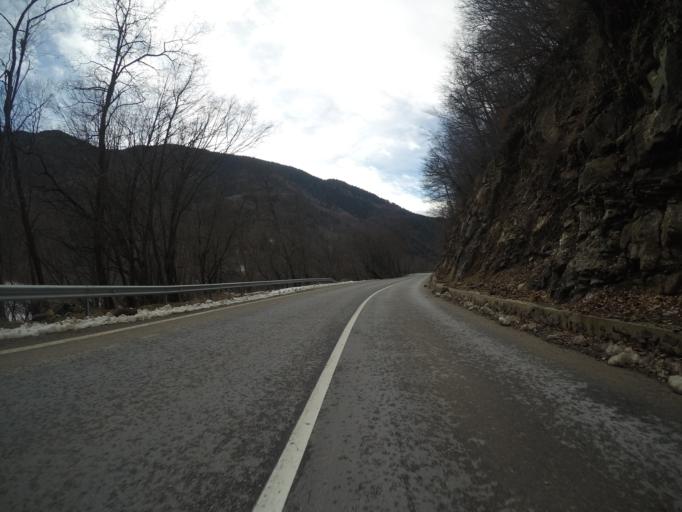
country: BG
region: Kyustendil
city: Sapareva Banya
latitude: 42.1141
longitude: 23.3198
